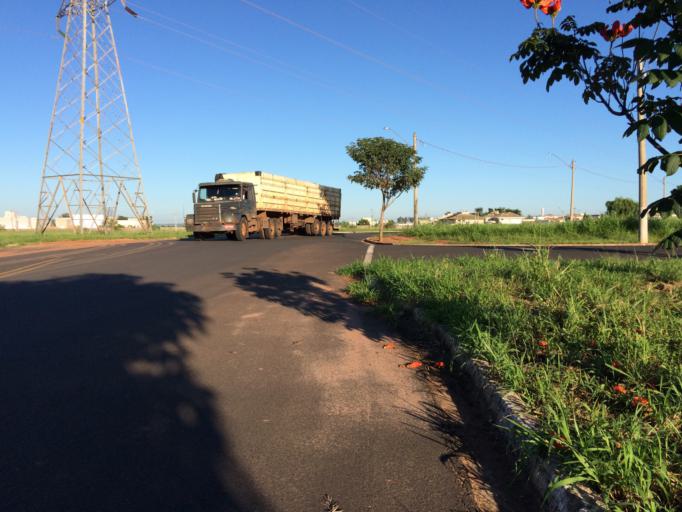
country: BR
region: Sao Paulo
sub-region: Matao
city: Matao
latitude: -21.6247
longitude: -48.3592
